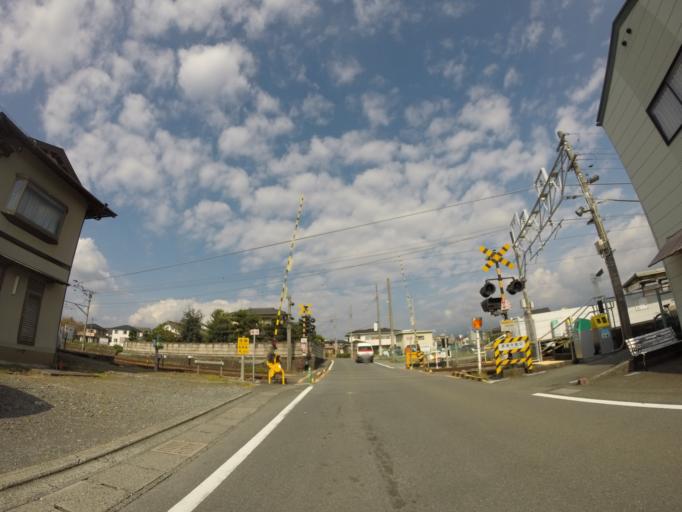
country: JP
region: Shizuoka
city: Fujinomiya
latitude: 35.2145
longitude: 138.6266
